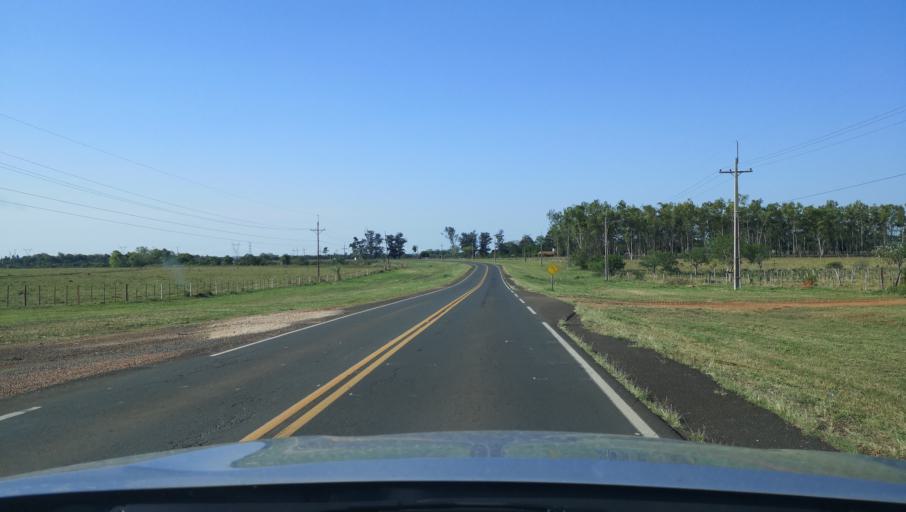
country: PY
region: Misiones
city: Santa Maria
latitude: -26.8102
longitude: -57.0213
